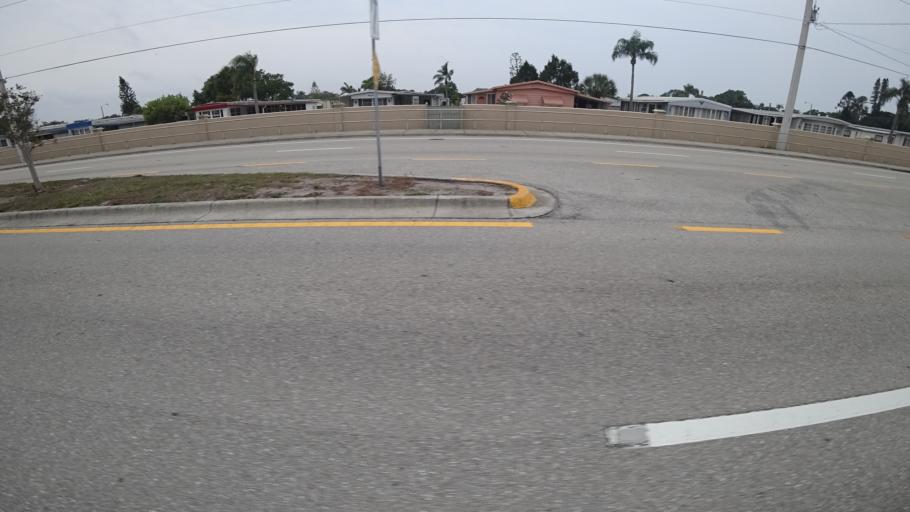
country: US
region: Florida
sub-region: Manatee County
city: Whitfield
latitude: 27.4294
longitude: -82.5656
